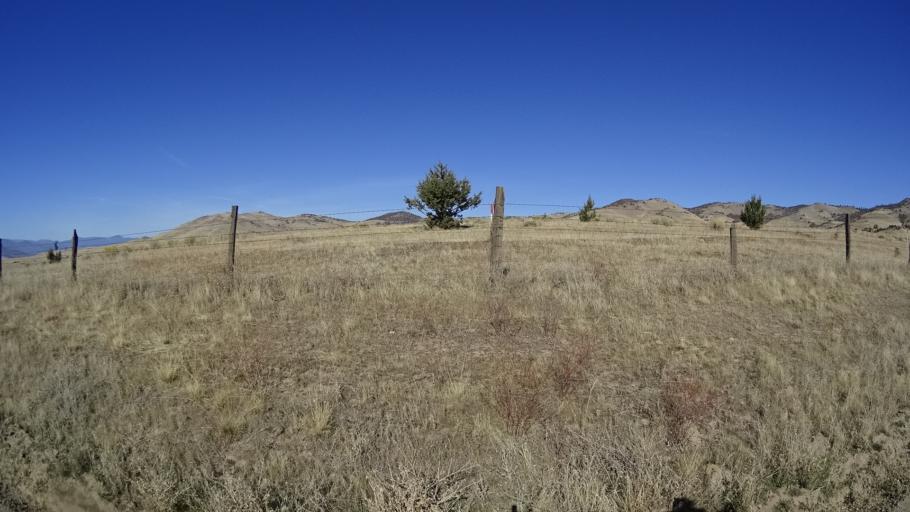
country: US
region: California
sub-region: Siskiyou County
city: Montague
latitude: 41.8129
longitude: -122.3689
